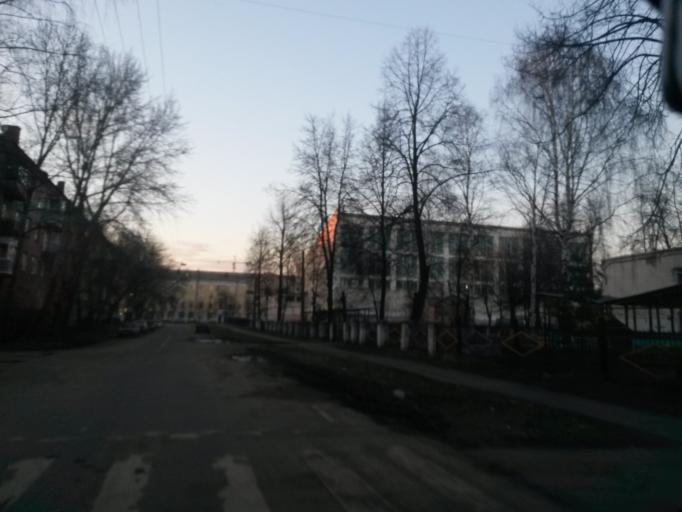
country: RU
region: Jaroslavl
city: Yaroslavl
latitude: 57.6361
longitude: 39.8424
